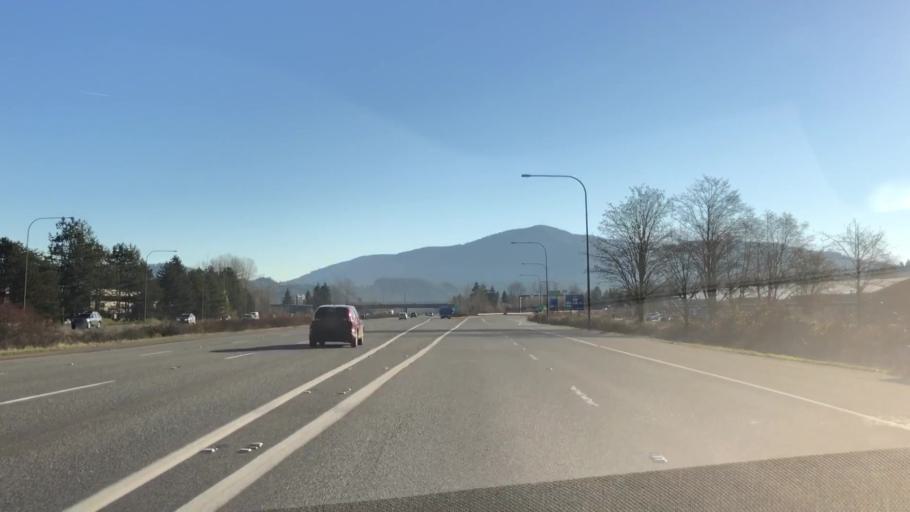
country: US
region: Washington
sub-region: King County
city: West Lake Sammamish
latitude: 47.5527
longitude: -122.0679
